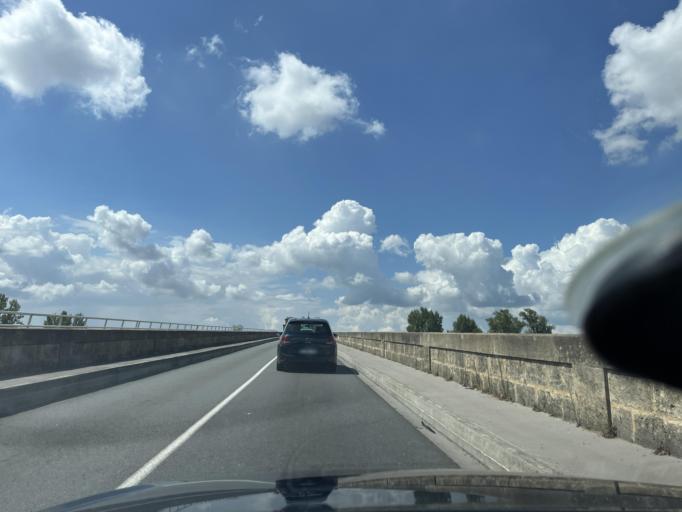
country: FR
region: Aquitaine
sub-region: Departement de la Gironde
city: Cubzac-les-Ponts
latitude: 44.9641
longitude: -0.4566
